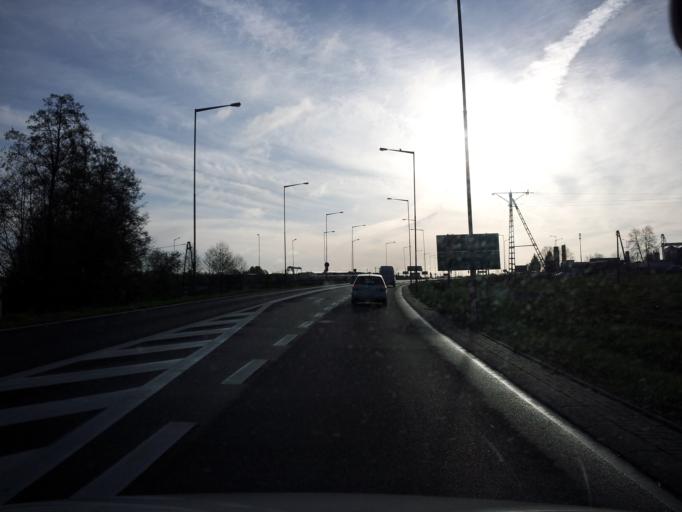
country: PL
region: Lubusz
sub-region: Powiat zarski
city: Zary
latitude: 51.6540
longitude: 15.1213
